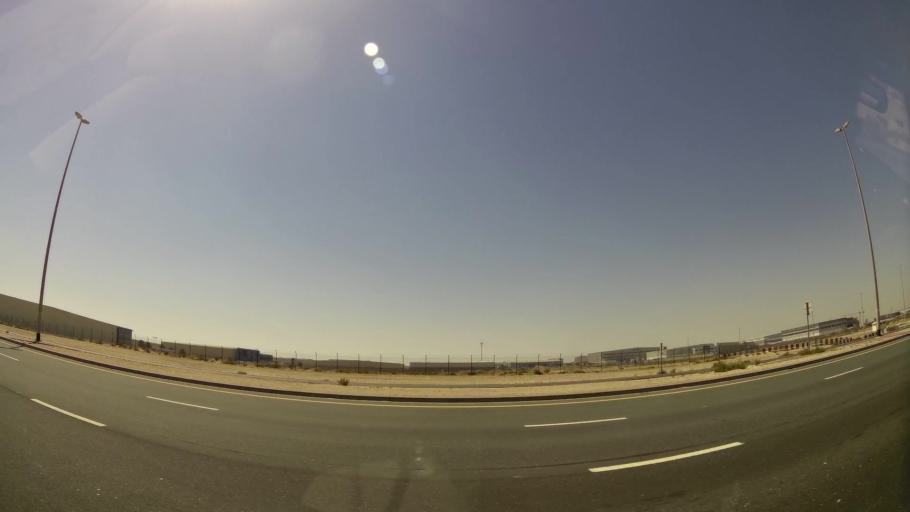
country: AE
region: Dubai
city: Dubai
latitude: 24.9421
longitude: 55.1054
